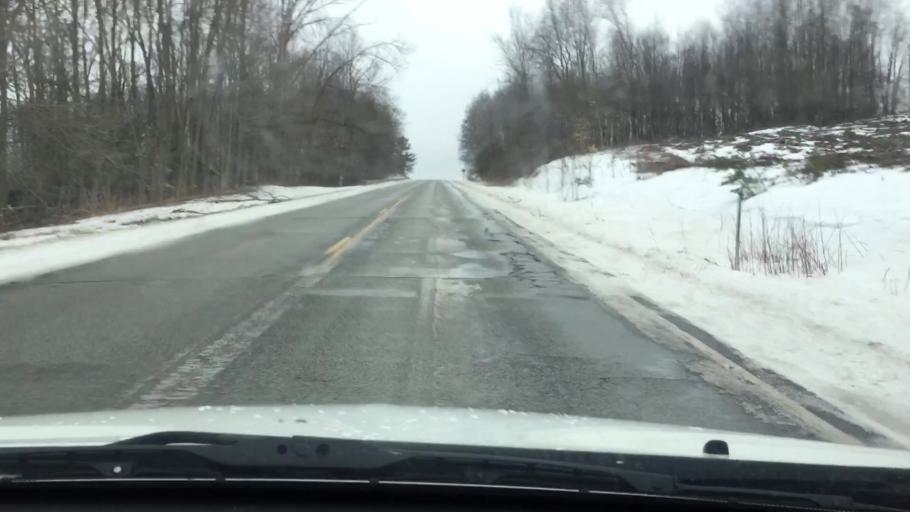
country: US
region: Michigan
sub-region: Wexford County
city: Cadillac
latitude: 44.1693
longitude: -85.4054
